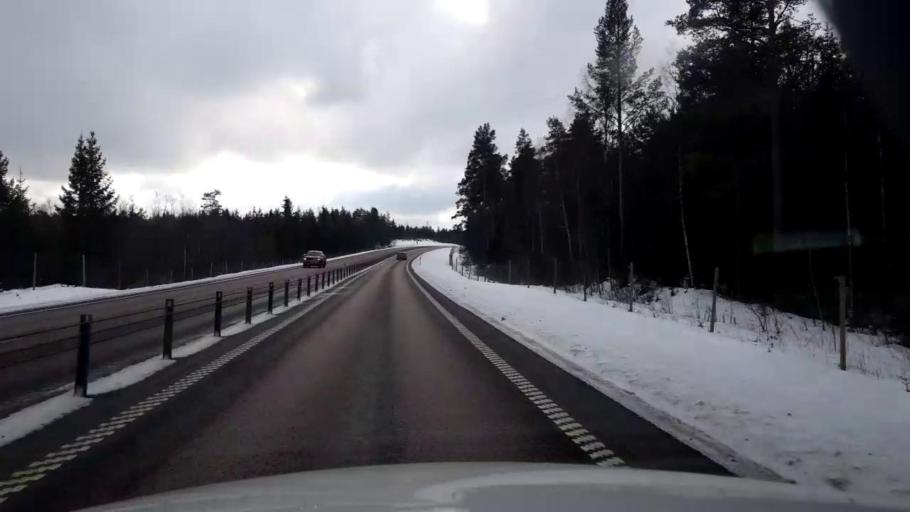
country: SE
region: Gaevleborg
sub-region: Hudiksvalls Kommun
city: Hudiksvall
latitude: 61.8144
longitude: 17.1892
